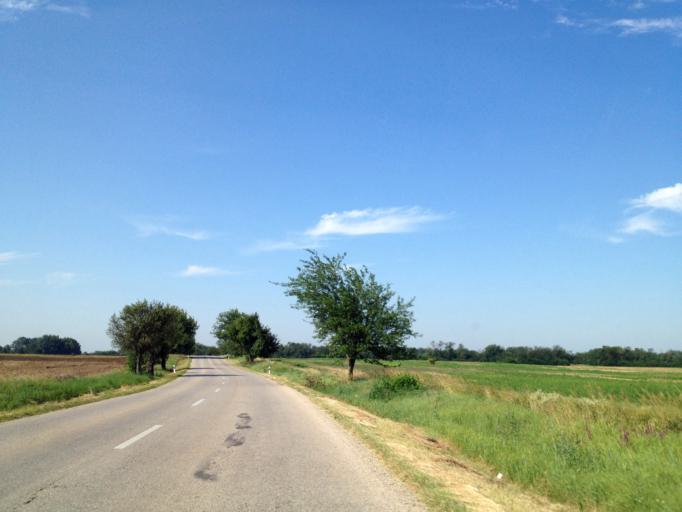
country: SK
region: Nitriansky
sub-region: Okres Komarno
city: Hurbanovo
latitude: 47.8223
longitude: 18.2301
